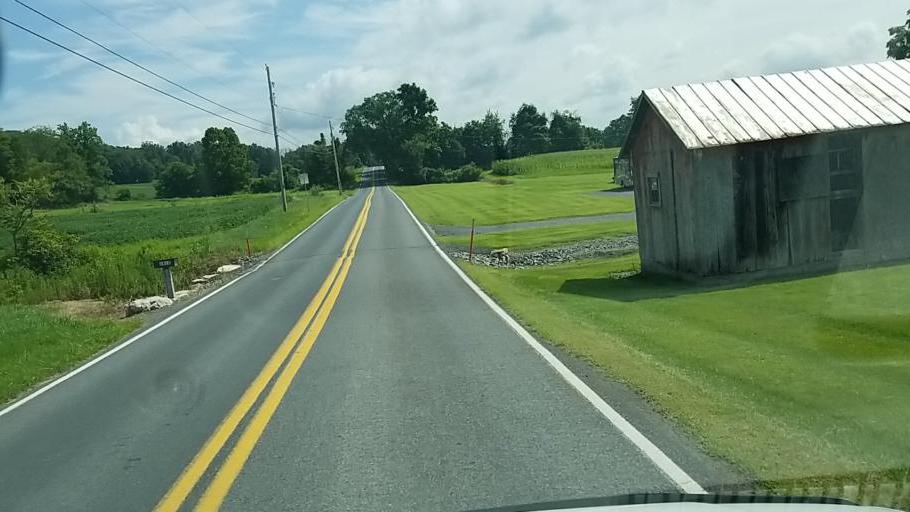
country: US
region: Pennsylvania
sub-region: Dauphin County
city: Millersburg
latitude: 40.5804
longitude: -76.9324
